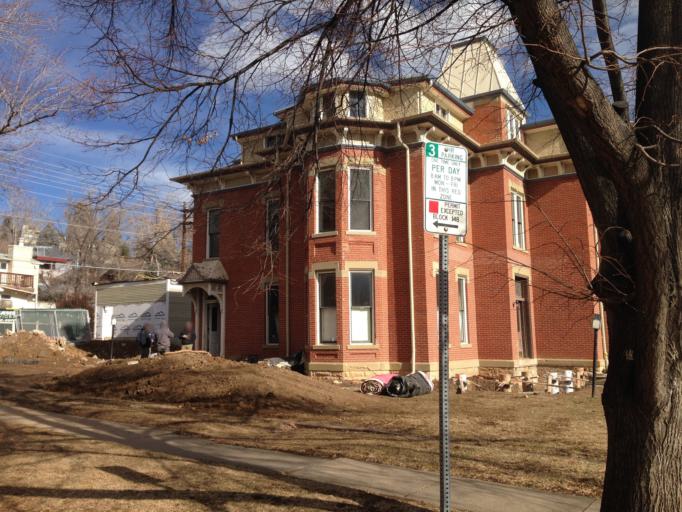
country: US
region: Colorado
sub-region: Boulder County
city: Boulder
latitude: 40.0209
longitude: -105.2768
